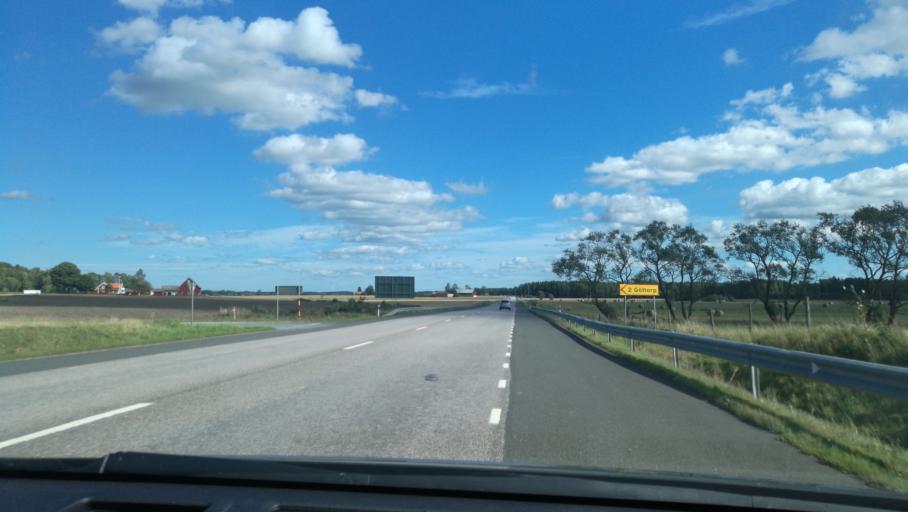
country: SE
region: Vaestra Goetaland
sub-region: Gotene Kommun
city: Goetene
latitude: 58.5112
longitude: 13.4098
